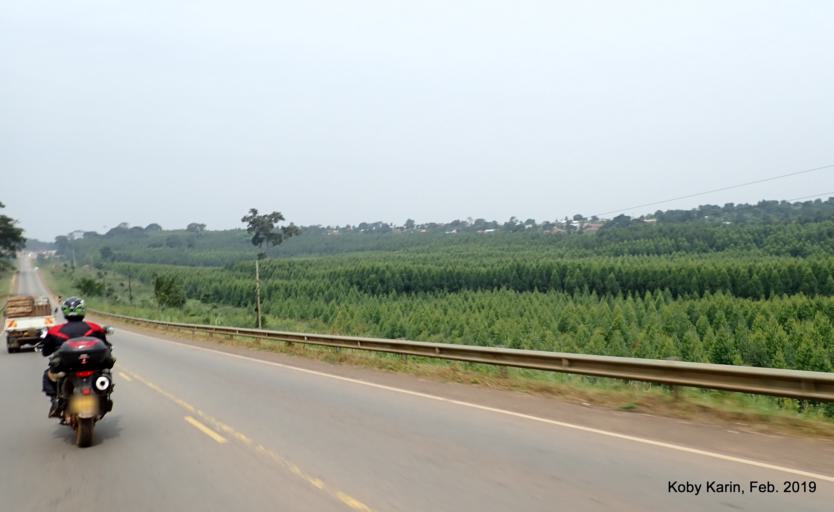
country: UG
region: Central Region
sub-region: Wakiso District
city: Wakiso
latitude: 0.3300
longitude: 32.3865
